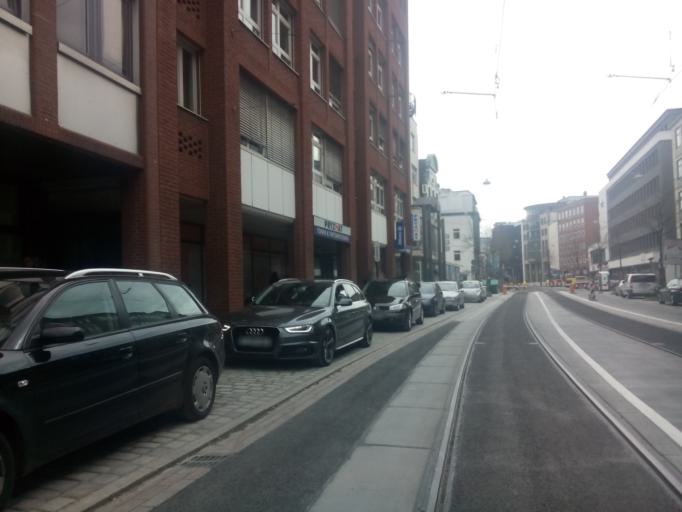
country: DE
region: Bremen
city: Bremen
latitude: 53.0802
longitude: 8.7980
